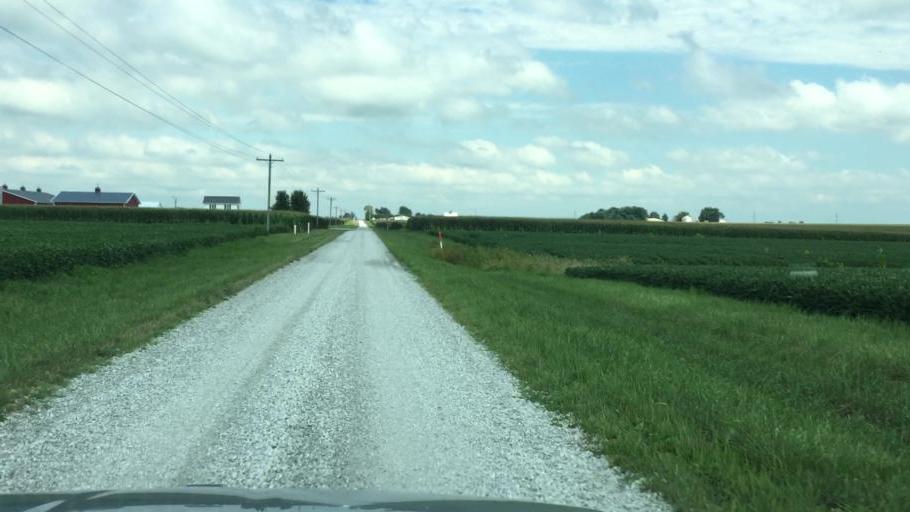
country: US
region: Illinois
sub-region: Hancock County
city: Nauvoo
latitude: 40.5214
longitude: -91.2801
